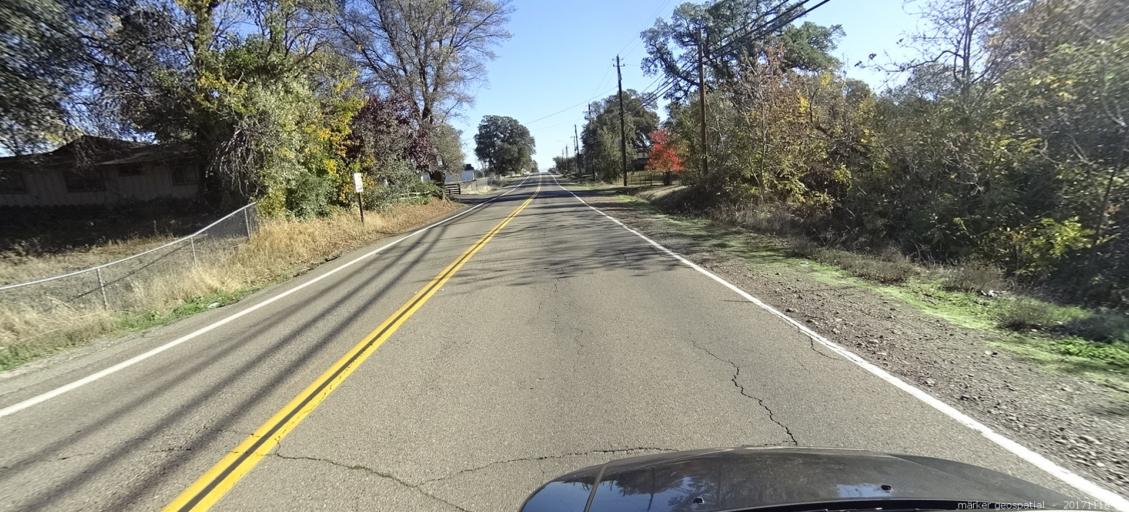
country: US
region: California
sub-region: Shasta County
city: Cottonwood
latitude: 40.3857
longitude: -122.2880
